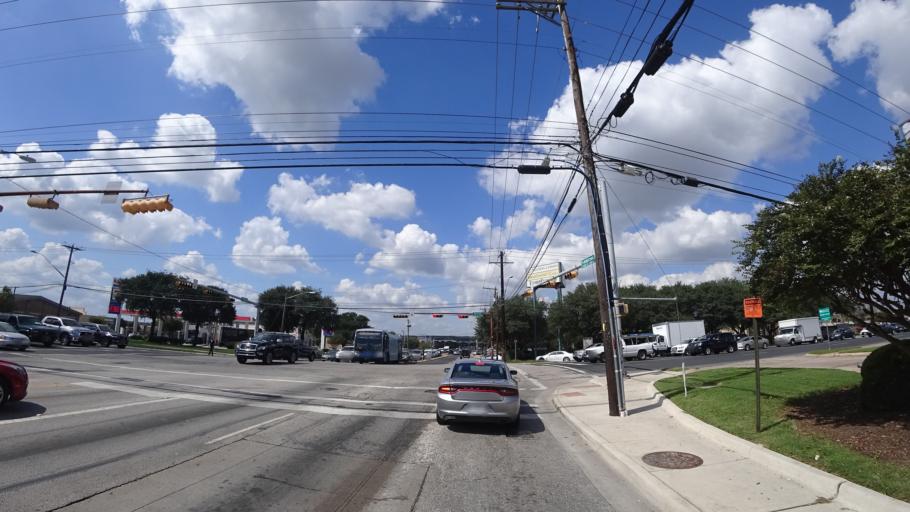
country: US
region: Texas
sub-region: Travis County
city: Austin
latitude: 30.3561
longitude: -97.7306
